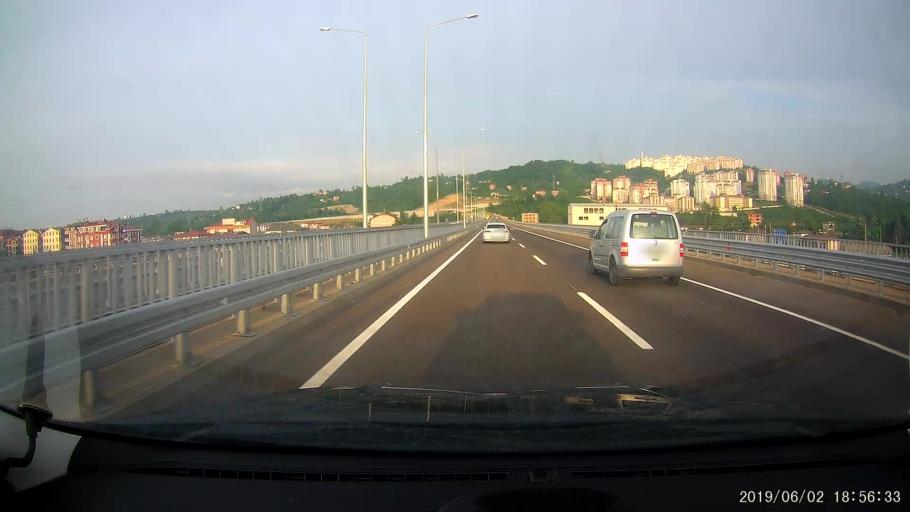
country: TR
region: Ordu
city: Ordu
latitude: 40.9552
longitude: 37.8937
